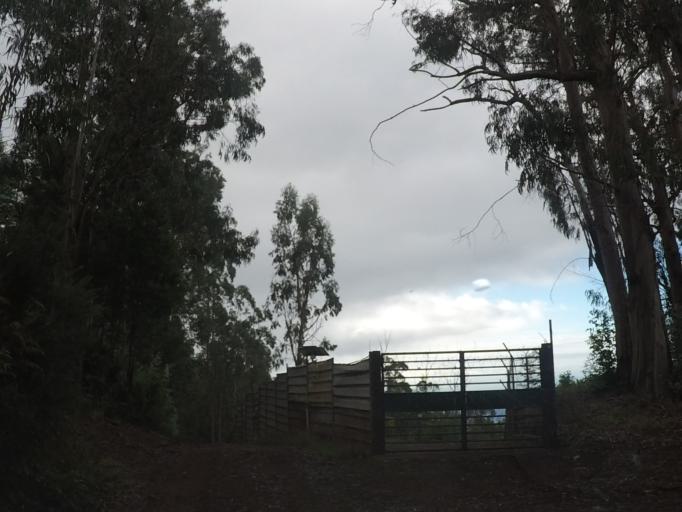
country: PT
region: Madeira
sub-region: Funchal
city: Nossa Senhora do Monte
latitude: 32.6781
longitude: -16.8777
